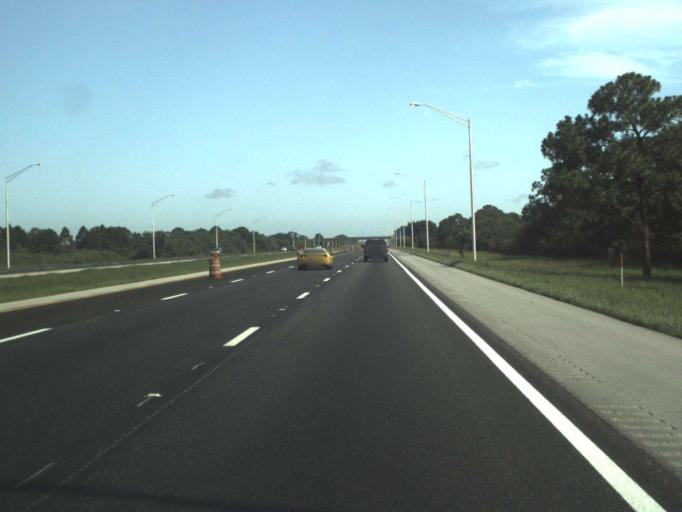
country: US
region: Florida
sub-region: Indian River County
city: West Vero Corridor
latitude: 27.5819
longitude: -80.4968
